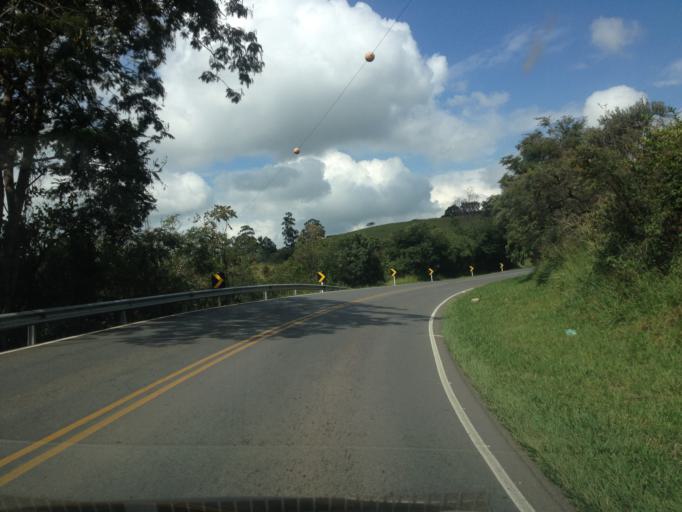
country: BR
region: Minas Gerais
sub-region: Itanhandu
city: Itanhandu
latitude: -22.2105
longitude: -44.9511
